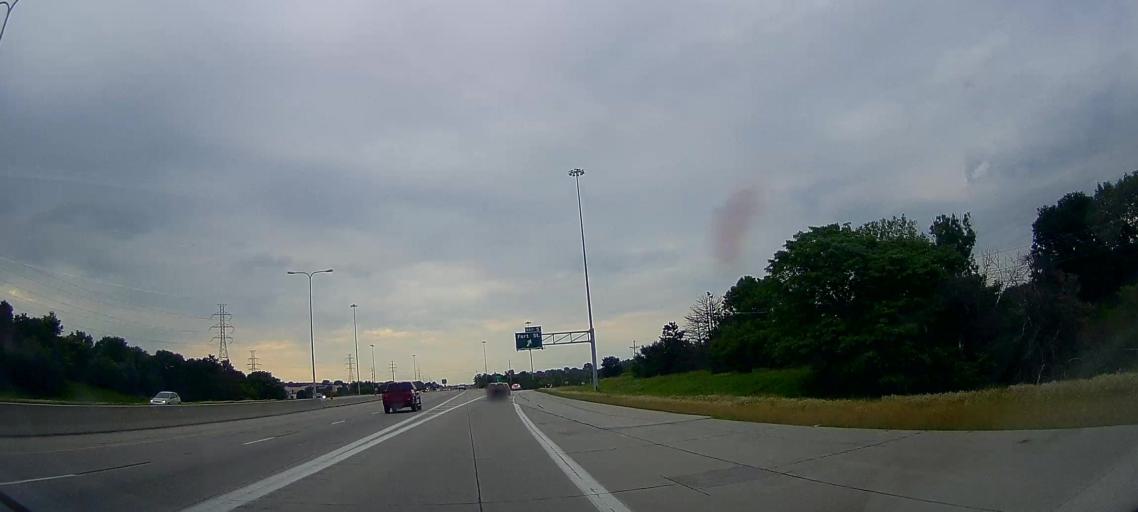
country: US
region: Nebraska
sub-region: Douglas County
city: Ralston
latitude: 41.3027
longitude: -96.0707
